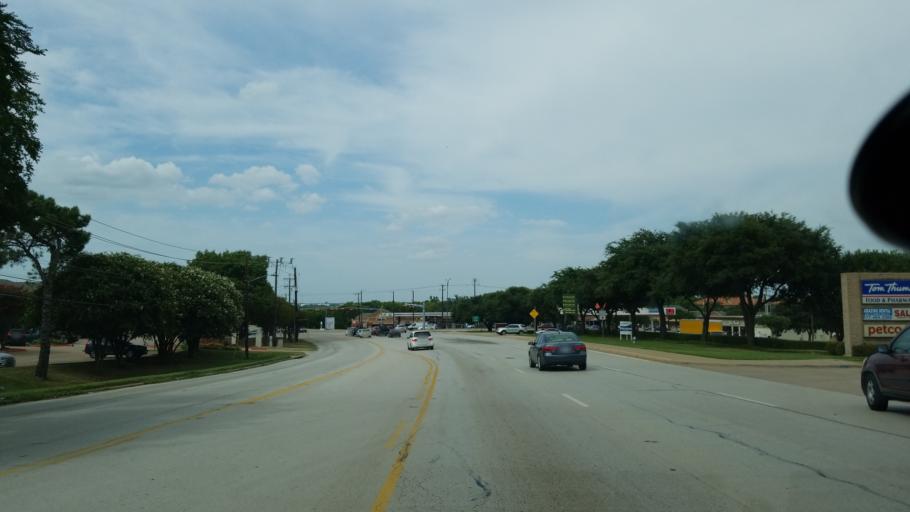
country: US
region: Texas
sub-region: Tarrant County
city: Arlington
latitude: 32.7830
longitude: -97.0956
